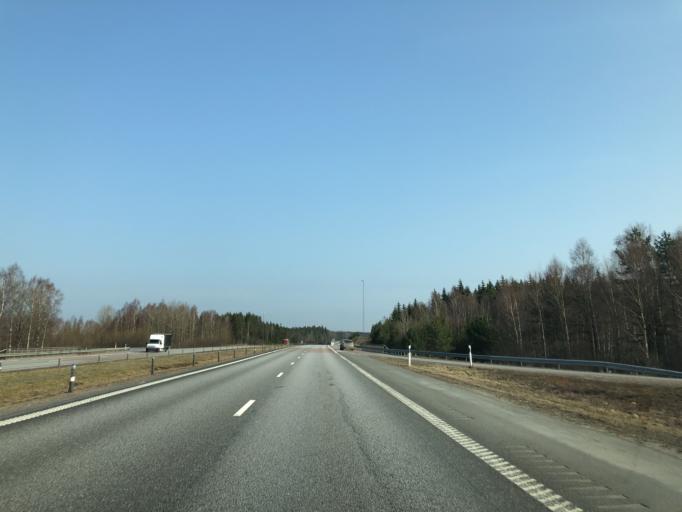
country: SE
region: Joenkoeping
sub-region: Varnamo Kommun
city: Varnamo
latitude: 57.1978
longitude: 14.0817
